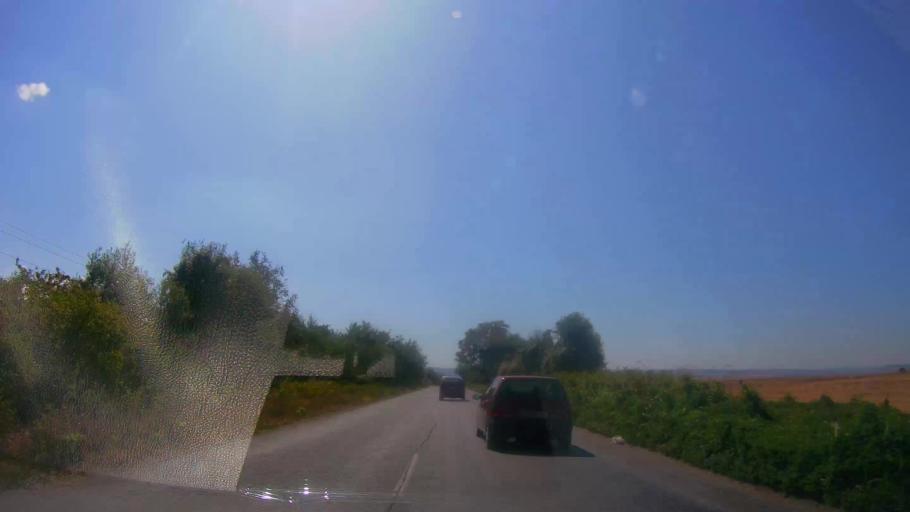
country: BG
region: Veliko Turnovo
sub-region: Obshtina Gorna Oryakhovitsa
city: Purvomaytsi
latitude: 43.2329
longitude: 25.6403
